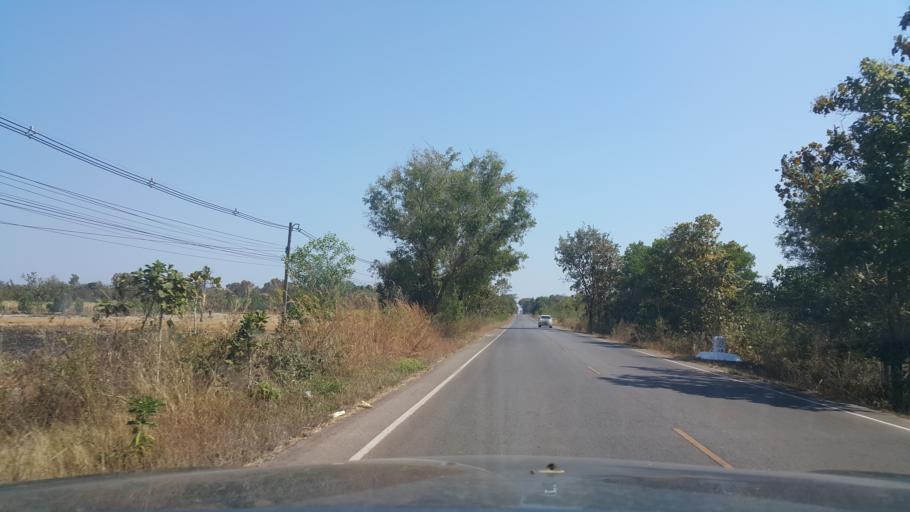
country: TH
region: Changwat Udon Thani
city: Ban Dung
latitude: 17.6084
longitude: 103.2559
